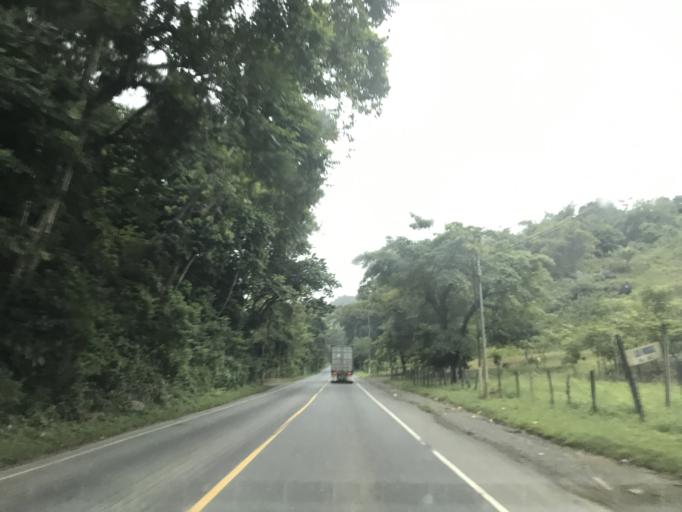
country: GT
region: Izabal
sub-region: Municipio de Puerto Barrios
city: Puerto Barrios
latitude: 15.6669
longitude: -88.5604
